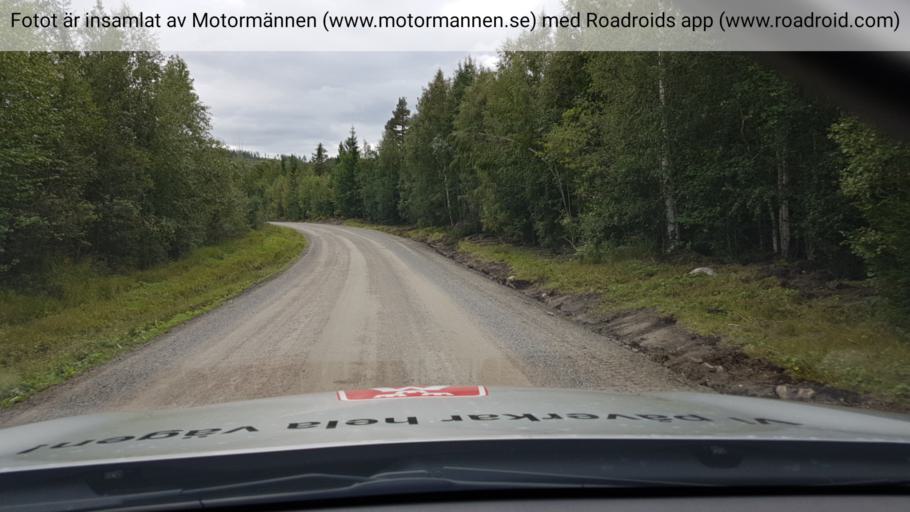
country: SE
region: Jaemtland
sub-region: Ragunda Kommun
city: Hammarstrand
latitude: 62.9275
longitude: 16.1248
